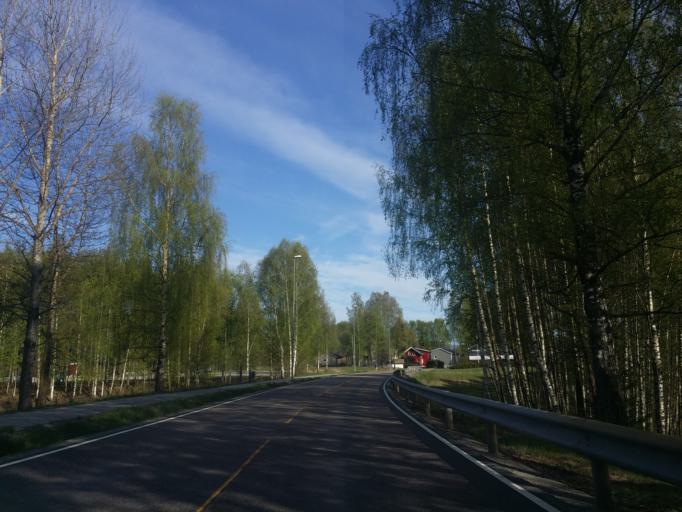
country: NO
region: Telemark
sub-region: Notodden
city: Notodden
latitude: 59.5918
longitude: 9.1503
